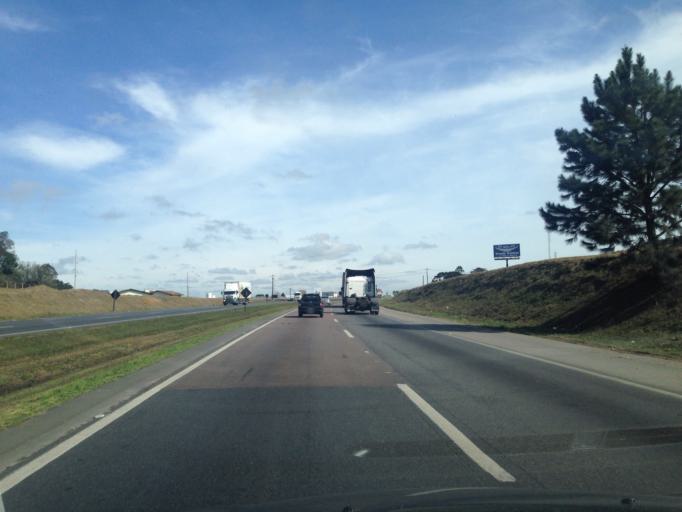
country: BR
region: Parana
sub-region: Sao Jose Dos Pinhais
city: Sao Jose dos Pinhais
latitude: -25.5640
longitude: -49.1561
